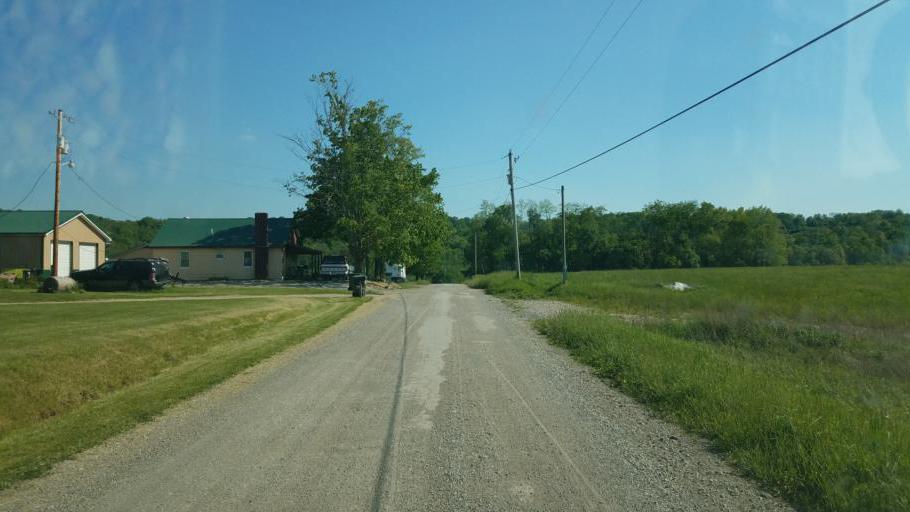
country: US
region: Ohio
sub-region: Belmont County
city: Barnesville
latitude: 40.0532
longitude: -81.3397
